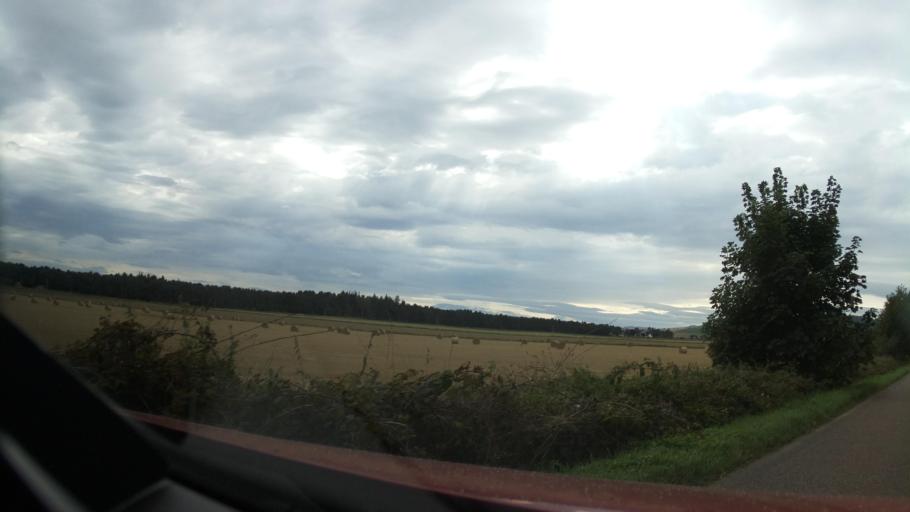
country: GB
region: Scotland
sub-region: Fife
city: Leuchars
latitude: 56.4093
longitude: -2.8961
